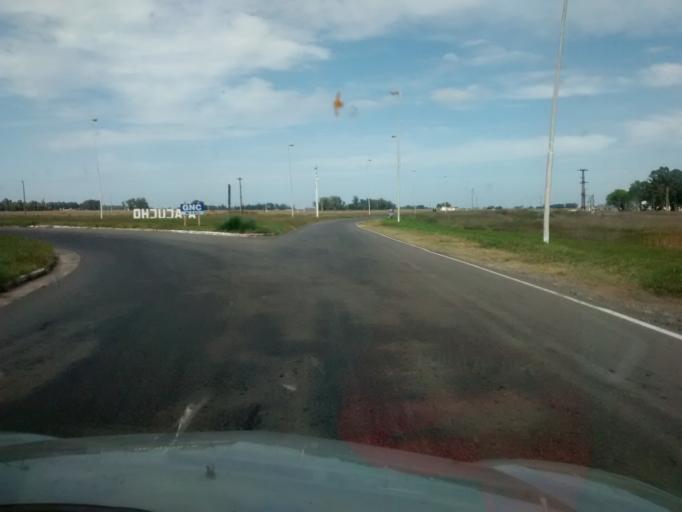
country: AR
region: Buenos Aires
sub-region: Partido de Ayacucho
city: Ayacucho
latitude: -37.1273
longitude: -58.5518
